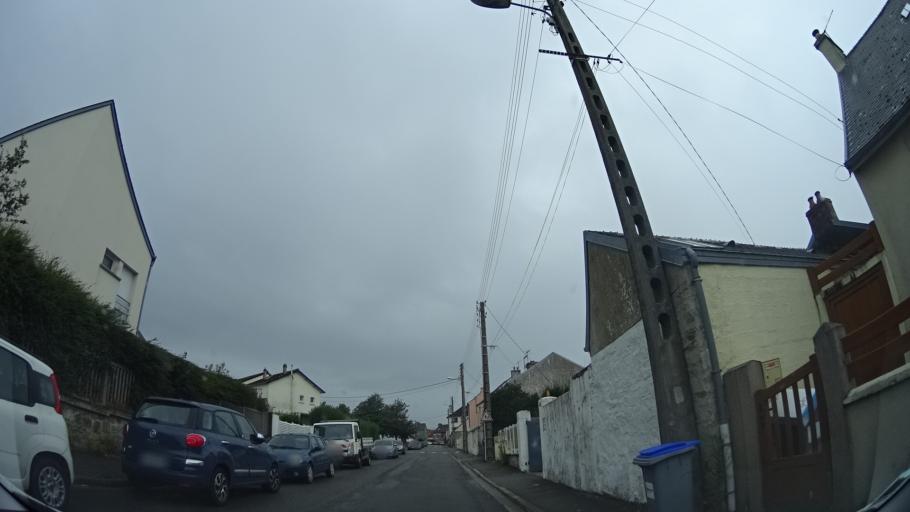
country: FR
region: Lower Normandy
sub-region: Departement de la Manche
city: Octeville
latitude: 49.6320
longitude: -1.6358
